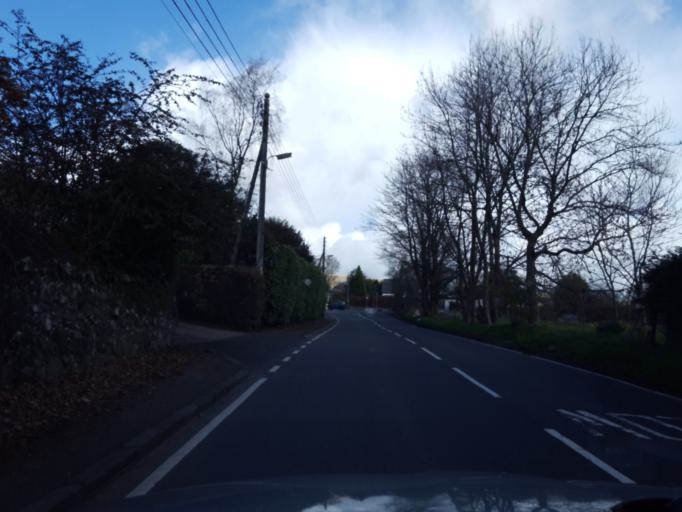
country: GB
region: Scotland
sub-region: Clackmannanshire
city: Dollar
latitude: 56.1944
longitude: -3.6060
